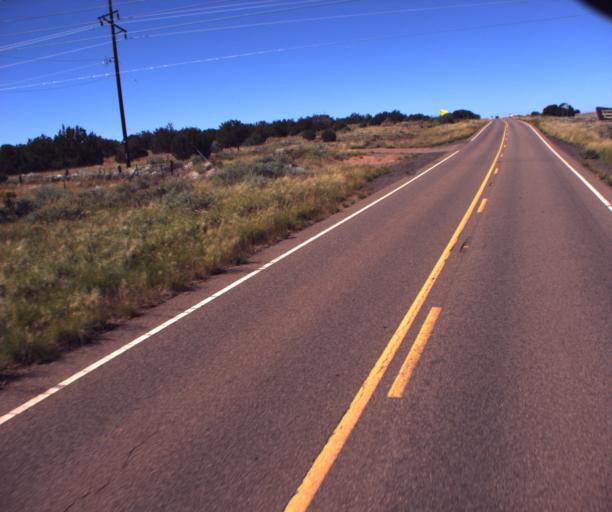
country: US
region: Arizona
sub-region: Navajo County
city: Taylor
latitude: 34.4832
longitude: -110.3251
